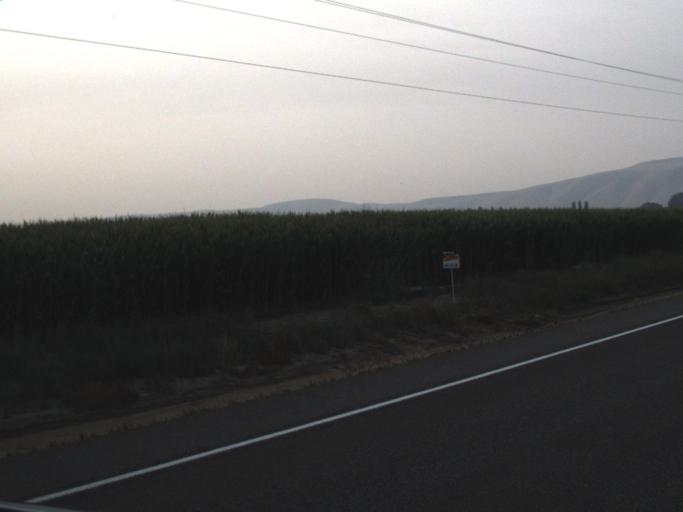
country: US
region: Washington
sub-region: Yakima County
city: Toppenish
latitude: 46.3491
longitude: -120.3205
